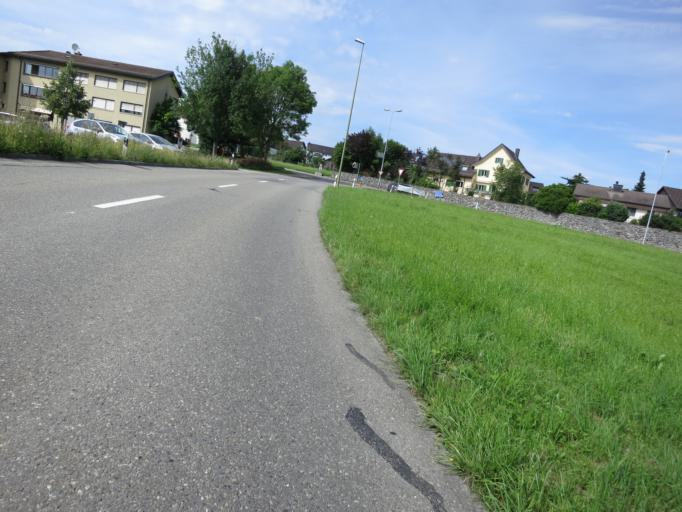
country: CH
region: Zurich
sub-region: Bezirk Meilen
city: Hombrechtikon
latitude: 47.2484
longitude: 8.7682
